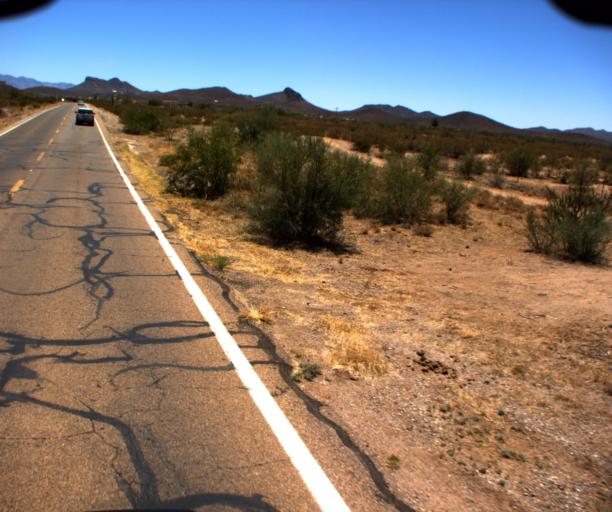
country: US
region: Arizona
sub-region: Pima County
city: Sells
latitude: 31.9276
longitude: -111.9027
